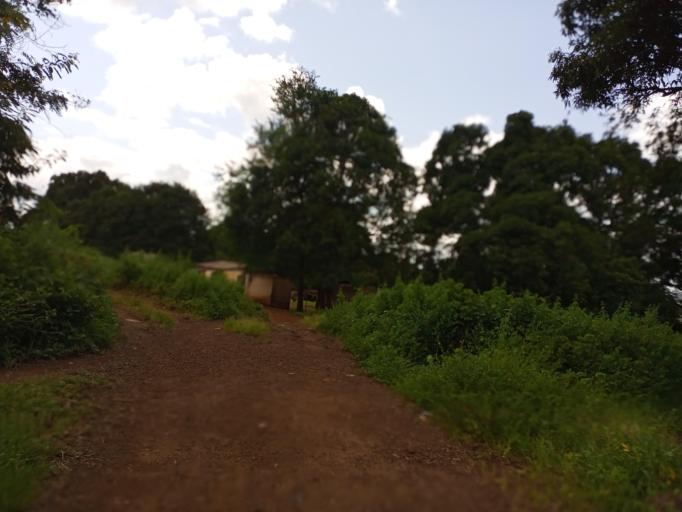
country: SL
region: Northern Province
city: Kamakwie
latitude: 9.4967
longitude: -12.2374
